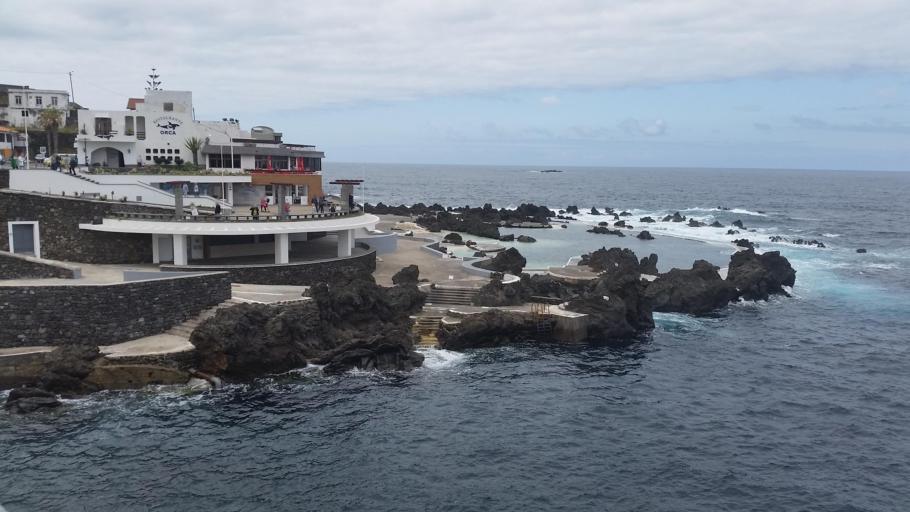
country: PT
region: Madeira
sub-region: Porto Moniz
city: Porto Moniz
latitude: 32.8678
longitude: -17.1694
